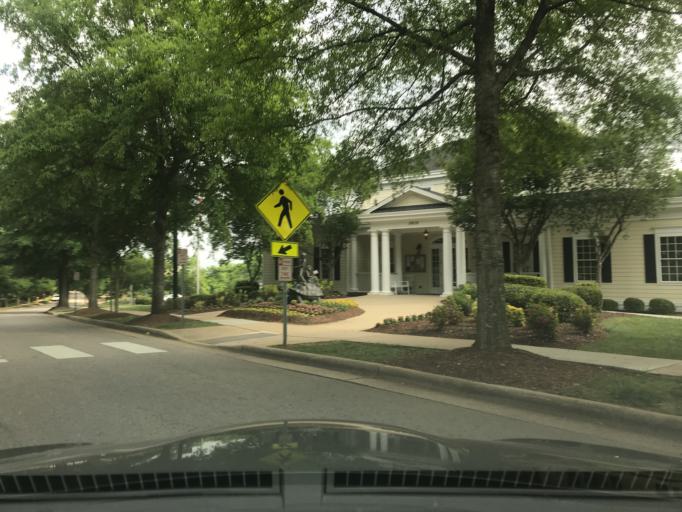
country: US
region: North Carolina
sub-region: Wake County
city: Wake Forest
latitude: 35.9260
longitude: -78.5659
